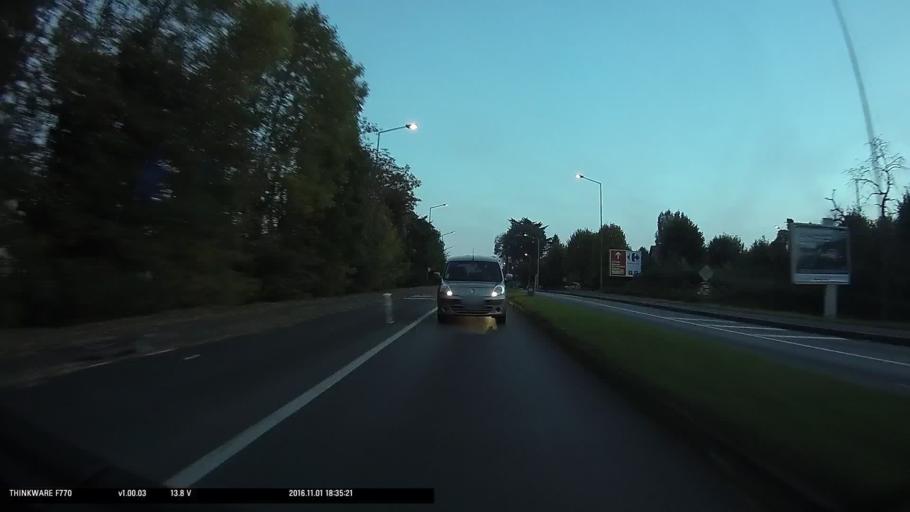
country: FR
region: Ile-de-France
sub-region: Departement de l'Essonne
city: Villemoisson-sur-Orge
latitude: 48.6656
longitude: 2.3398
